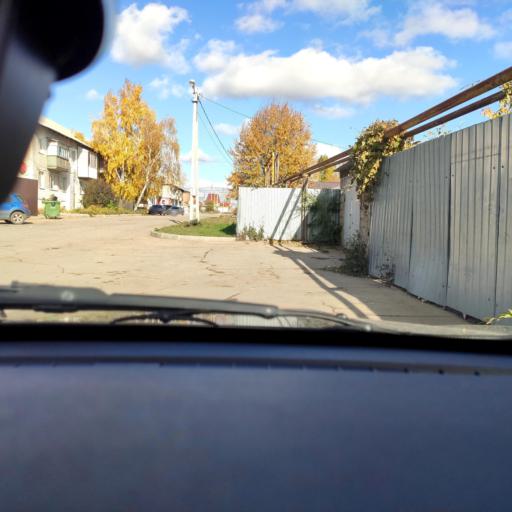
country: RU
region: Samara
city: Podstepki
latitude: 53.5107
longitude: 49.2306
